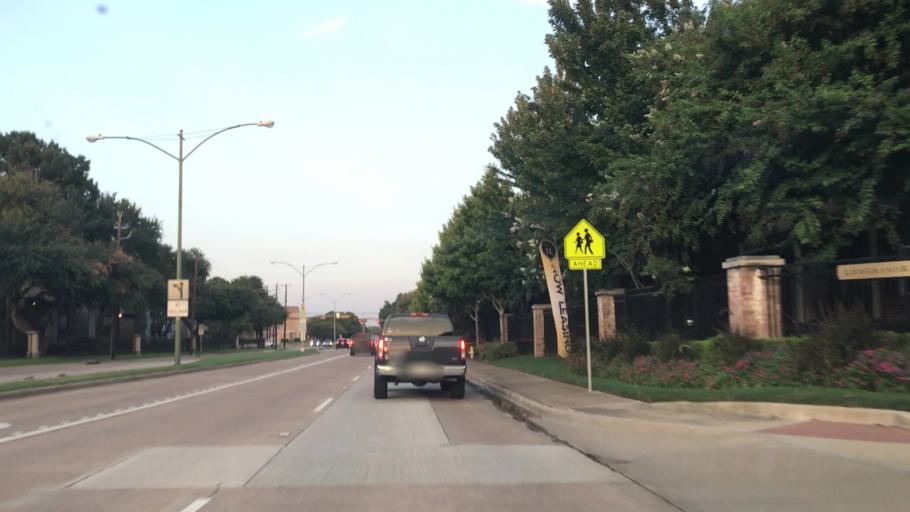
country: US
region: Texas
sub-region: Dallas County
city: Highland Park
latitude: 32.8508
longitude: -96.7626
